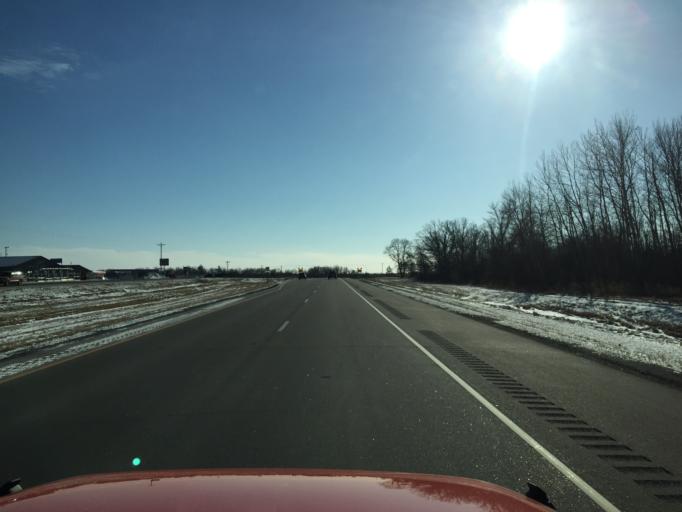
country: US
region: Minnesota
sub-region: Mille Lacs County
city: Milaca
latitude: 45.8266
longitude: -93.6584
